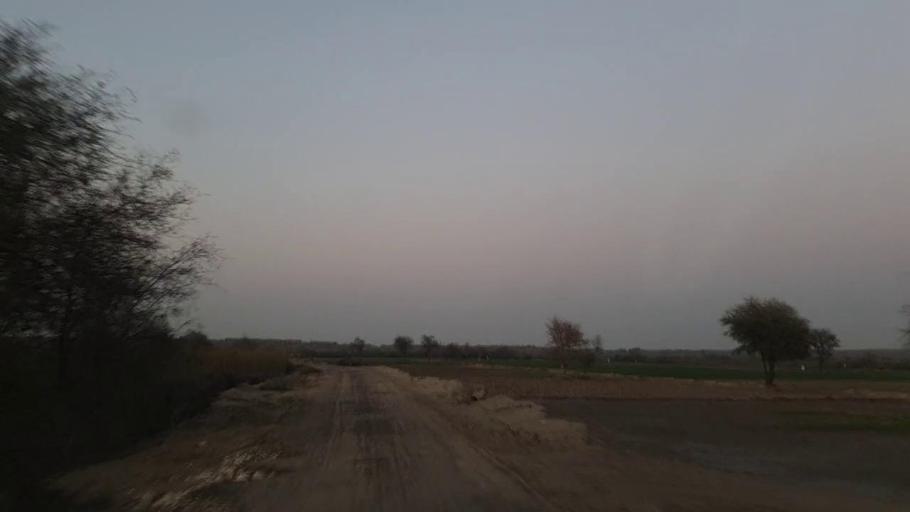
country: PK
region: Sindh
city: Bandhi
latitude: 26.6182
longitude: 68.3937
